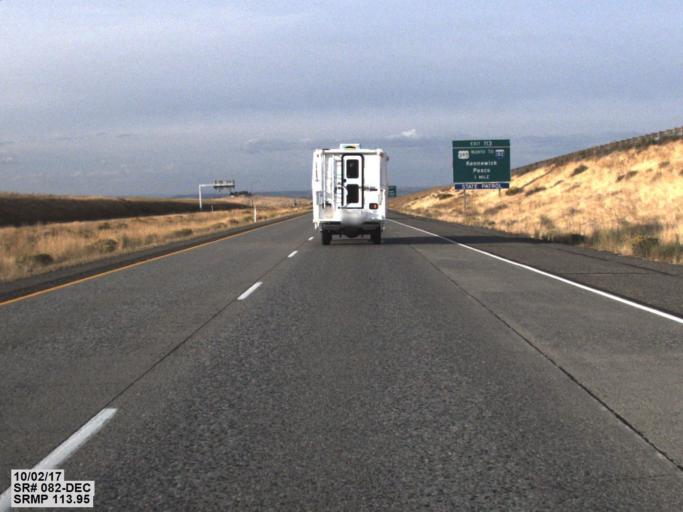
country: US
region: Washington
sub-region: Benton County
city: Highland
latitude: 46.1489
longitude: -119.2017
